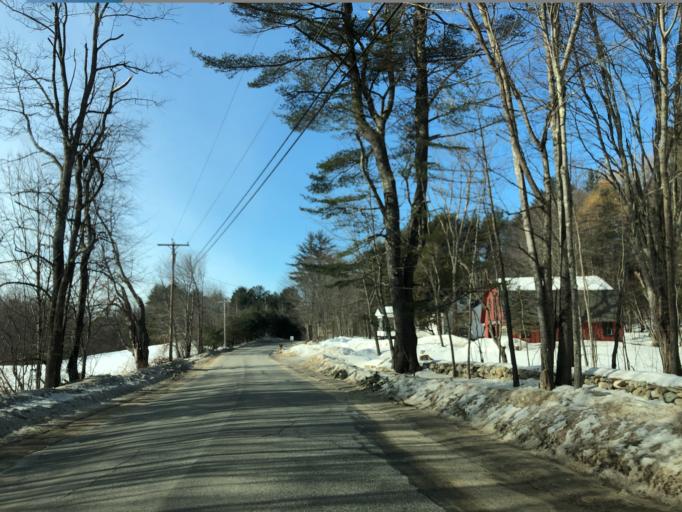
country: US
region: Maine
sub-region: Oxford County
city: Buckfield
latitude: 44.2965
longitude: -70.3733
